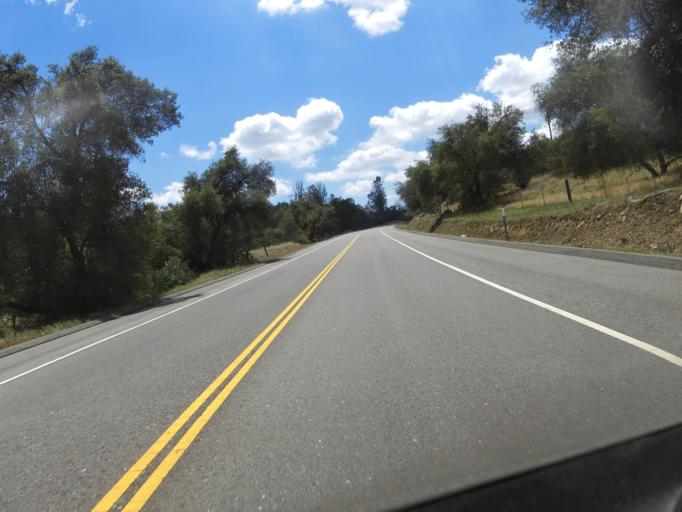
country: US
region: California
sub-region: Madera County
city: Coarsegold
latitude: 37.1582
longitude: -119.6458
